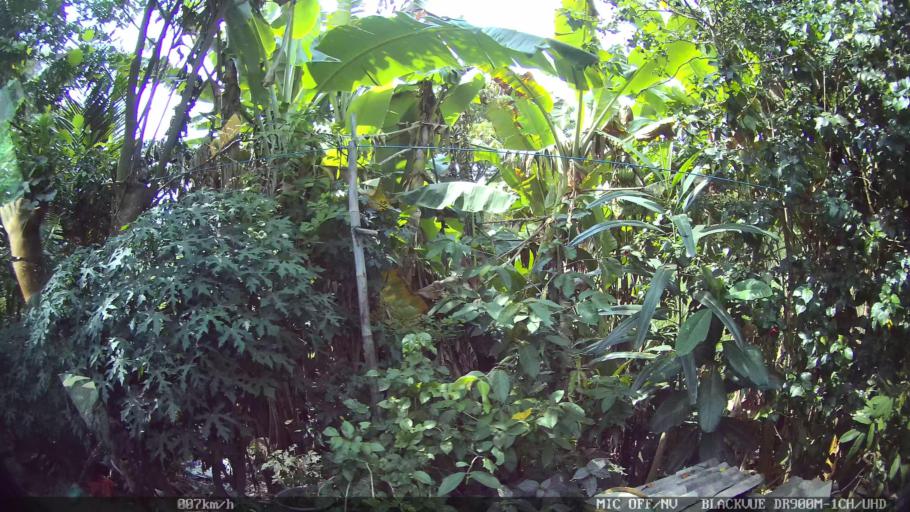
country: ID
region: Daerah Istimewa Yogyakarta
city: Yogyakarta
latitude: -7.8098
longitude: 110.4066
